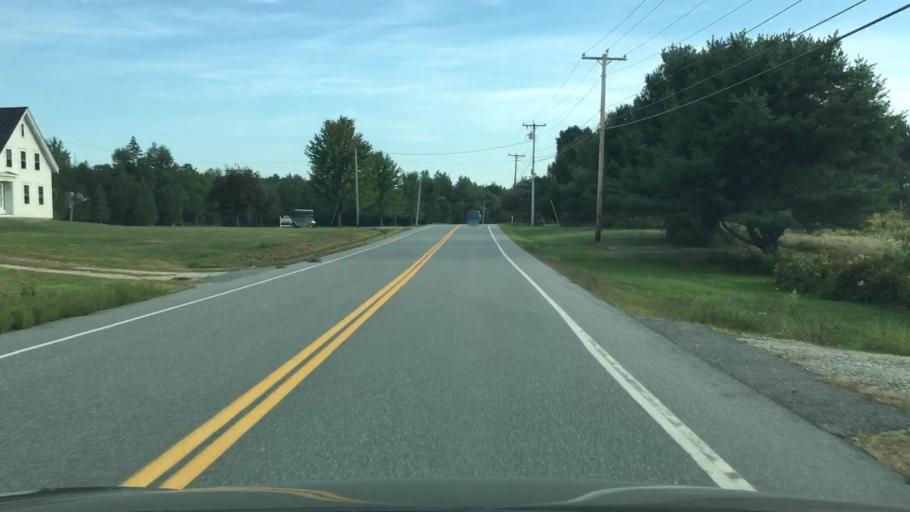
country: US
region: Maine
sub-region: Hancock County
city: Penobscot
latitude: 44.4590
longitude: -68.7804
